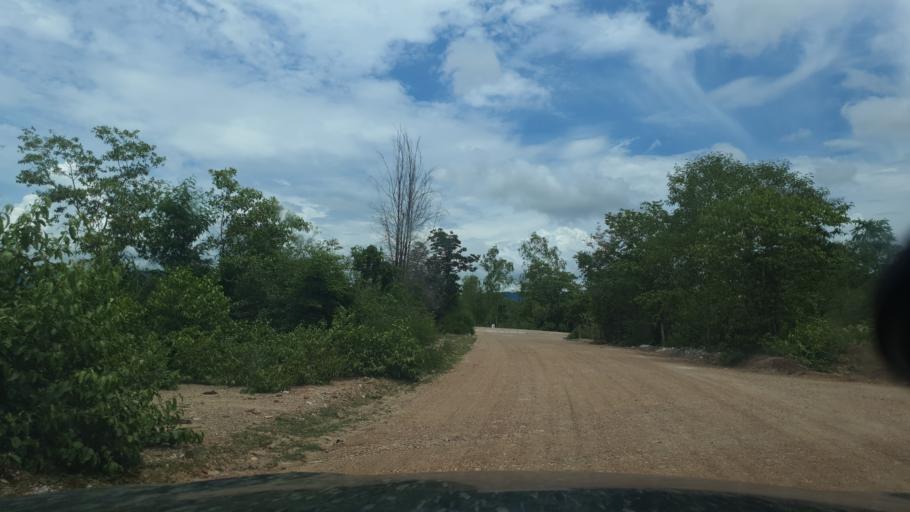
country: TH
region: Lampang
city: Sop Prap
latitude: 17.9344
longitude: 99.3647
